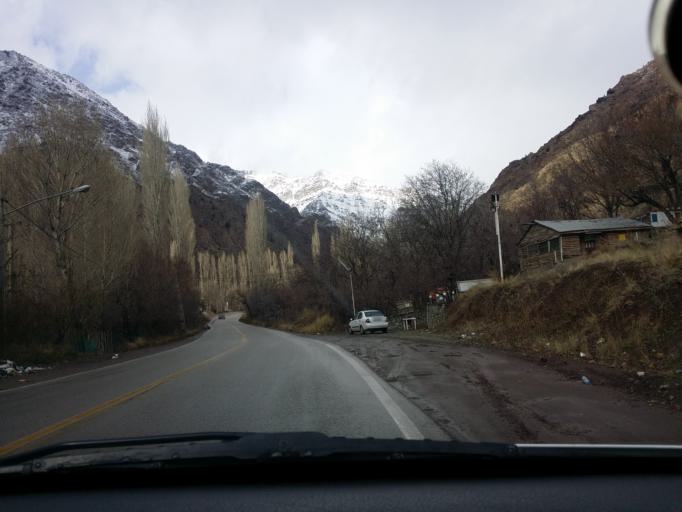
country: IR
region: Tehran
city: Tajrish
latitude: 36.0543
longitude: 51.3135
